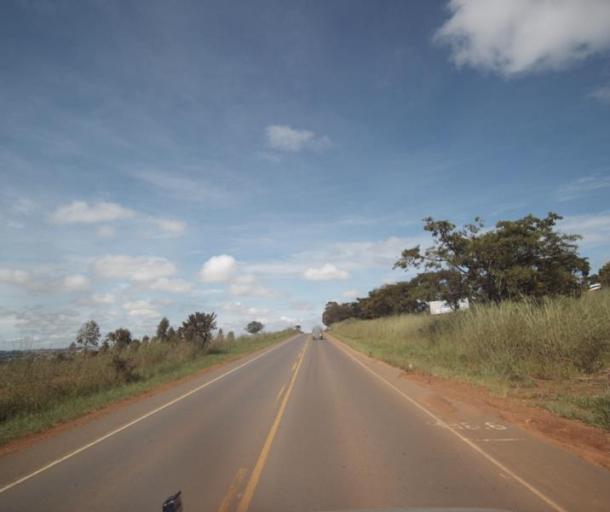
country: BR
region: Goias
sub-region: Anapolis
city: Anapolis
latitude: -16.2548
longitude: -48.9361
